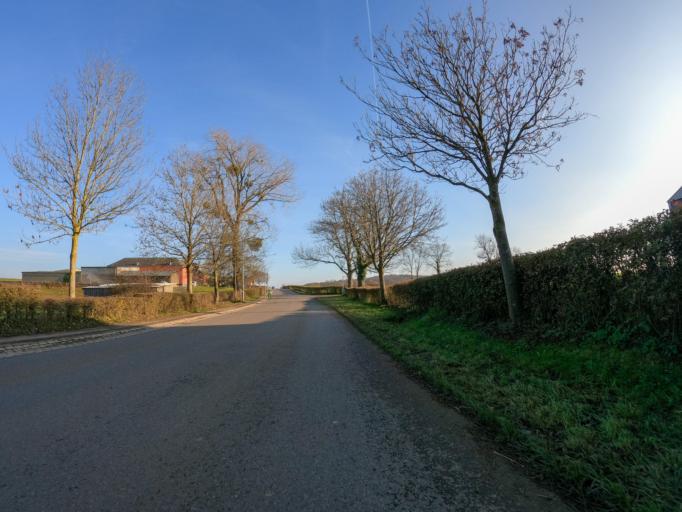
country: LU
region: Luxembourg
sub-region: Canton de Capellen
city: Garnich
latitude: 49.6017
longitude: 5.9296
